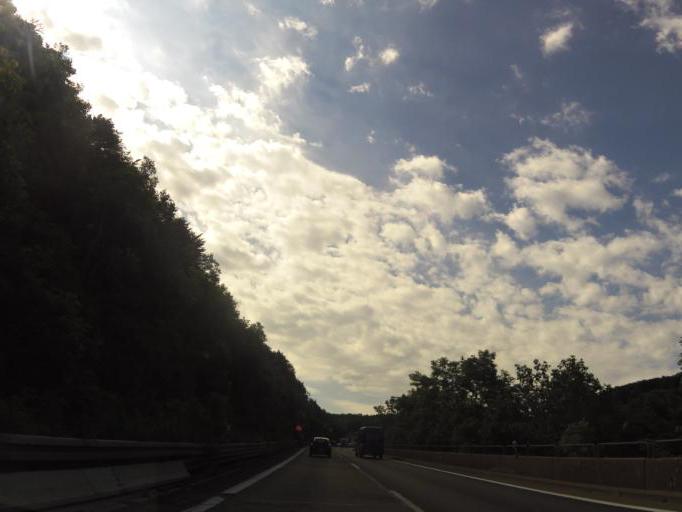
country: DE
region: Baden-Wuerttemberg
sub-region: Regierungsbezirk Stuttgart
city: Wiesensteig
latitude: 48.5557
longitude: 9.6309
